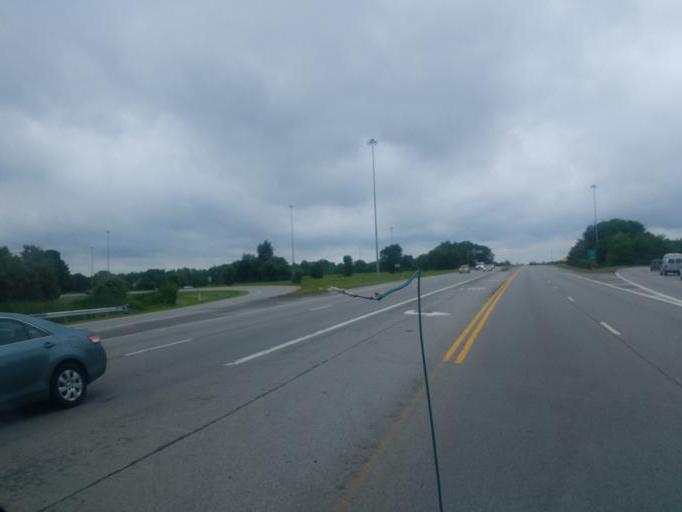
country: US
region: Ohio
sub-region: Franklin County
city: Whitehall
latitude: 39.9787
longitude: -82.8482
